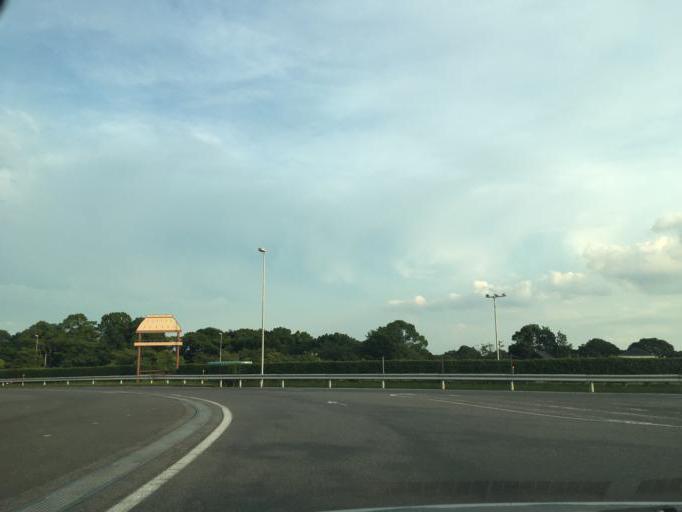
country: JP
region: Saga Prefecture
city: Kanzakimachi-kanzaki
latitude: 33.3298
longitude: 130.3119
